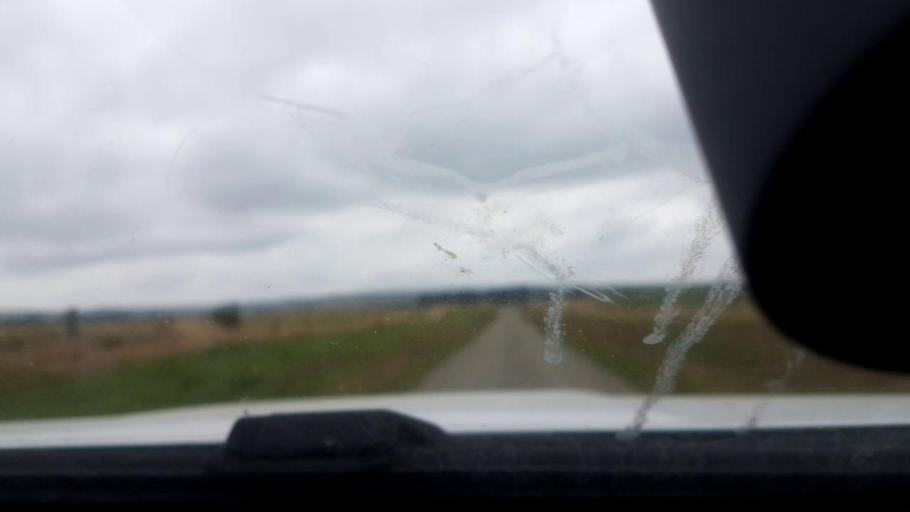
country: NZ
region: Canterbury
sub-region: Timaru District
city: Pleasant Point
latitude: -44.2318
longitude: 171.1668
